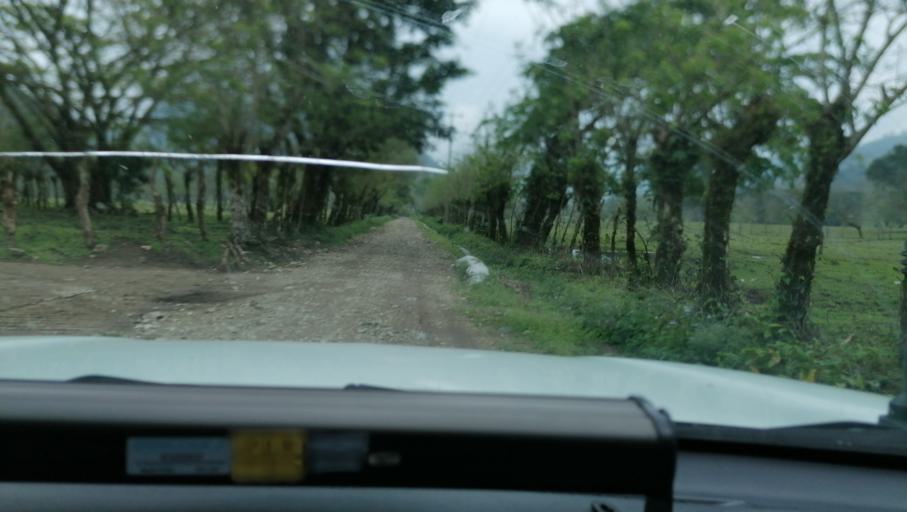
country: MX
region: Chiapas
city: Ixtacomitan
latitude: 17.3645
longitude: -93.1748
